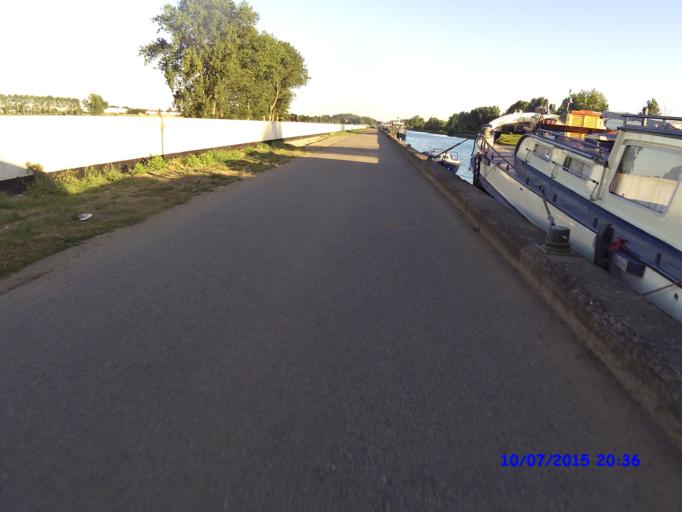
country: BE
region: Flanders
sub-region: Provincie Antwerpen
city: Rumst
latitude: 51.0596
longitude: 4.4321
